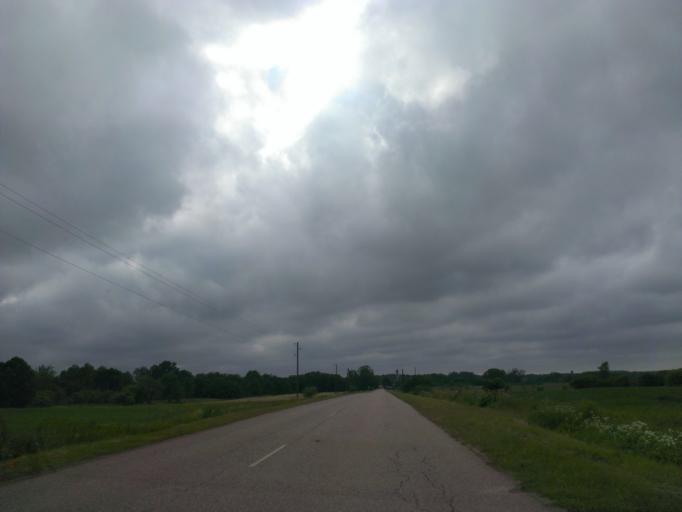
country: LV
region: Durbe
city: Liegi
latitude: 56.7278
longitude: 21.4101
